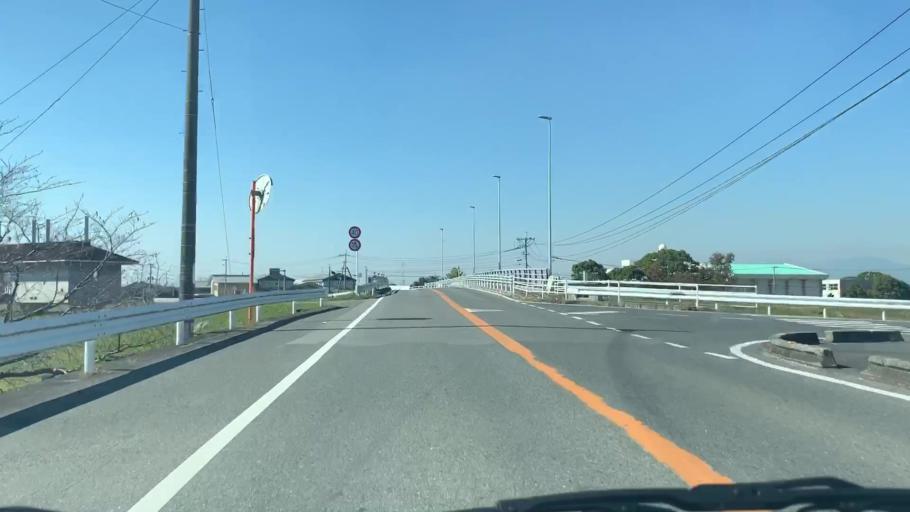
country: JP
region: Saga Prefecture
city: Kanzakimachi-kanzaki
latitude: 33.2623
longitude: 130.3957
